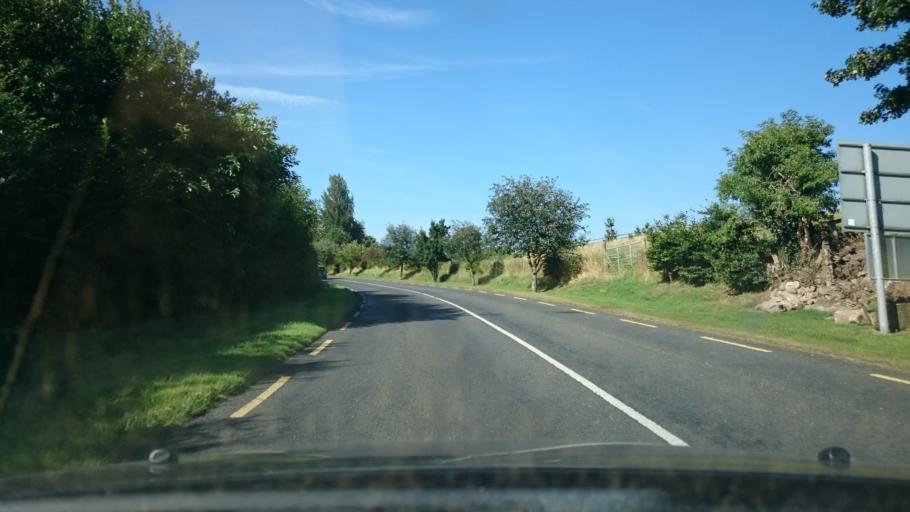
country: IE
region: Leinster
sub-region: Kilkenny
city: Graiguenamanagh
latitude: 52.5474
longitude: -6.9581
